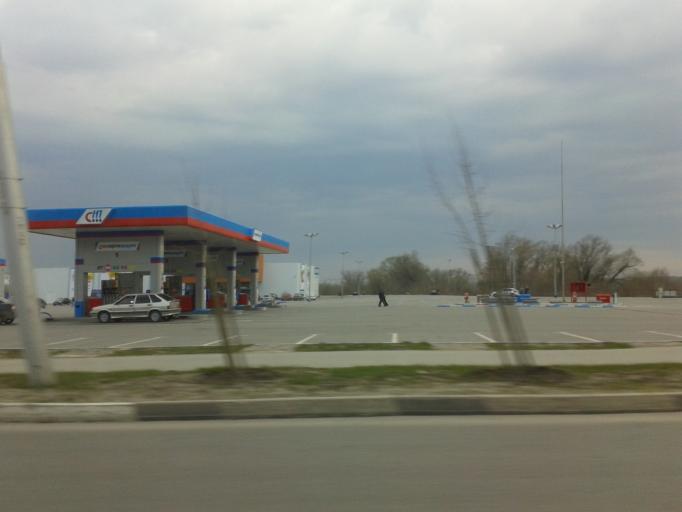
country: RU
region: Rjazan
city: Ryazan'
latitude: 54.6370
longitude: 39.6847
